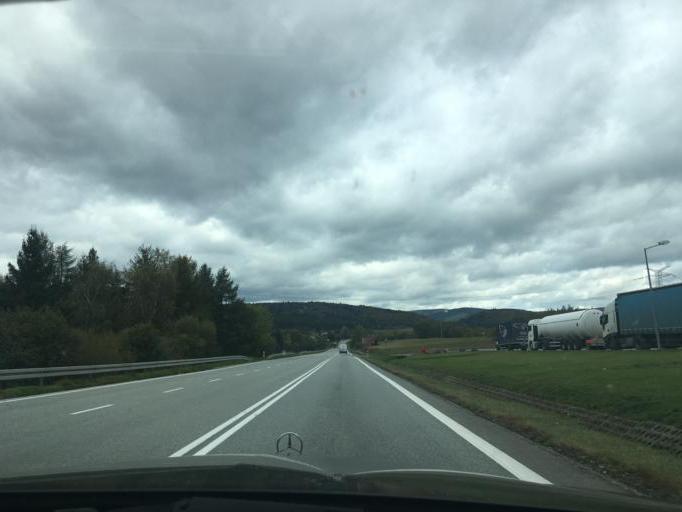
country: PL
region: Subcarpathian Voivodeship
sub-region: Powiat krosnienski
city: Jasliska
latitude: 49.4245
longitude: 21.6921
